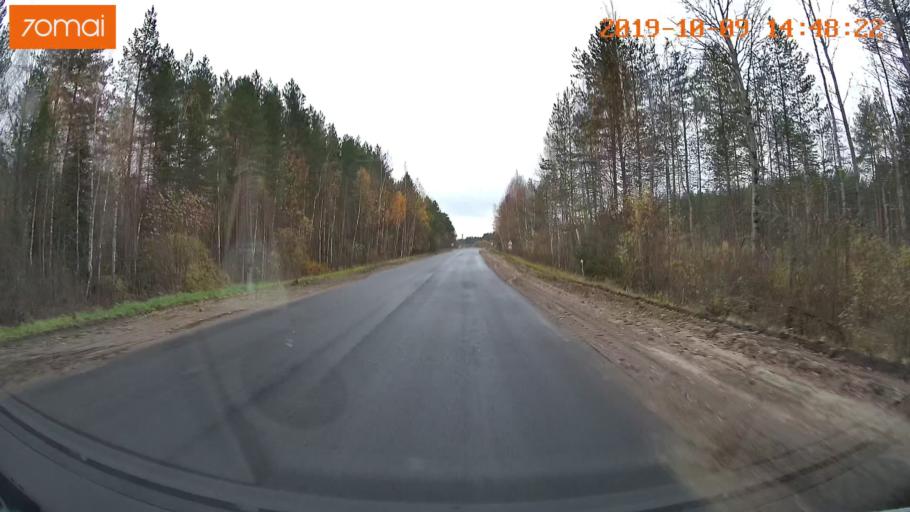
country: RU
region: Kostroma
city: Chistyye Bory
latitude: 58.4065
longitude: 41.5751
